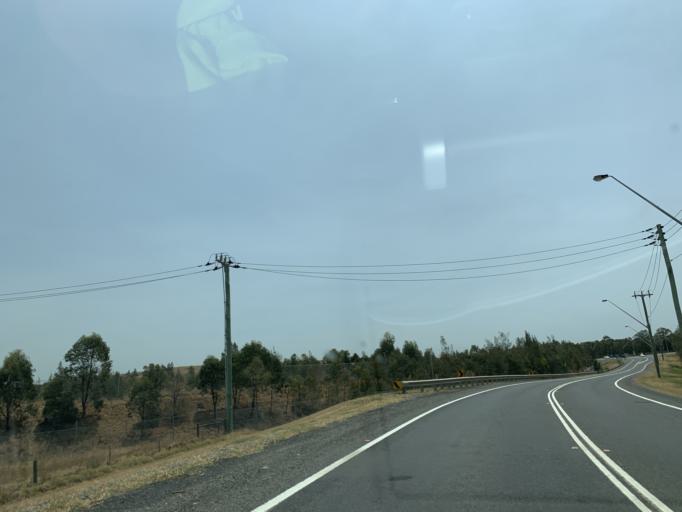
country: AU
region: New South Wales
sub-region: Fairfield
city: Horsley Park
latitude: -33.8207
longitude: 150.8670
